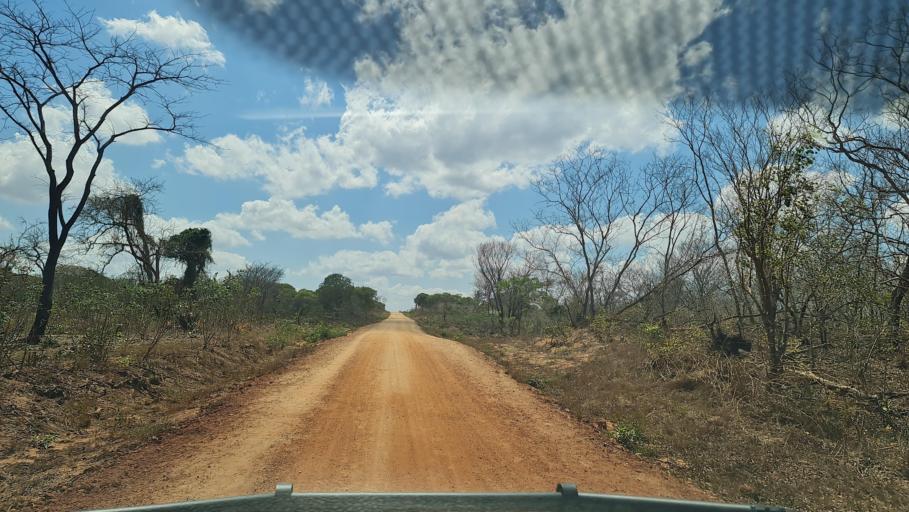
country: MZ
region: Nampula
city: Nacala
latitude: -14.1768
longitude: 40.2272
